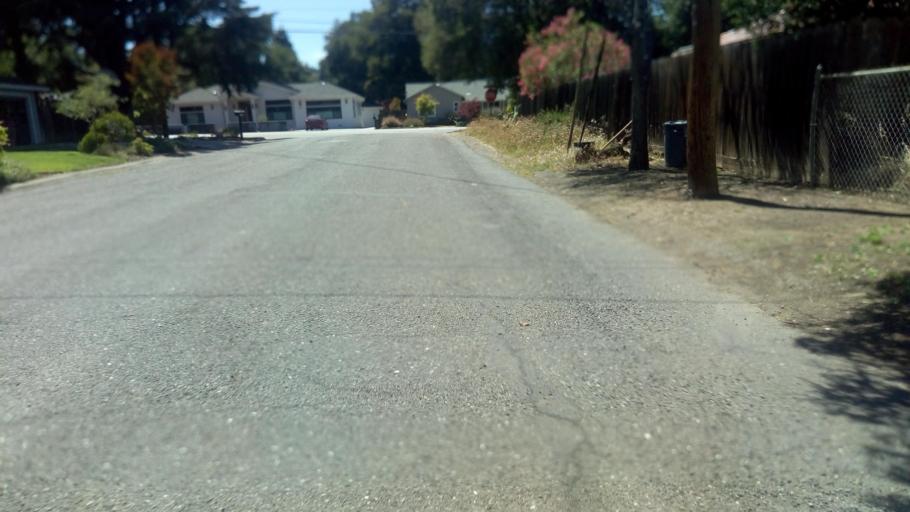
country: US
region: California
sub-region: Santa Clara County
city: Loyola
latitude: 37.3637
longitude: -122.0954
